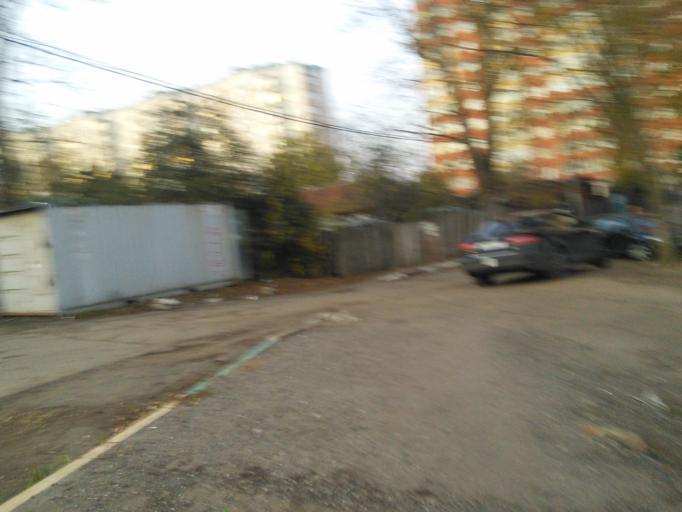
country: RU
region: Moskovskaya
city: Novopodrezkovo
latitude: 55.9377
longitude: 37.3501
